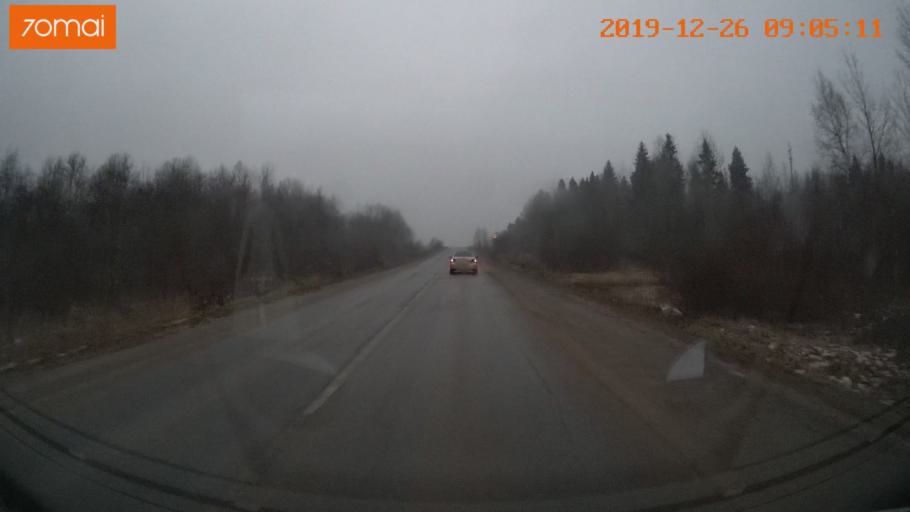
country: RU
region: Vologda
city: Gryazovets
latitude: 58.8229
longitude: 40.2592
